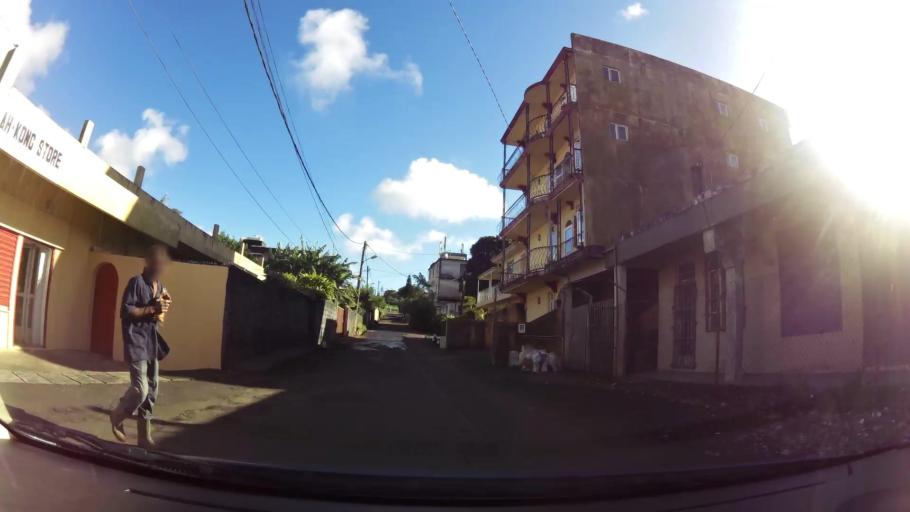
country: MU
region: Plaines Wilhems
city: Curepipe
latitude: -20.3161
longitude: 57.5348
